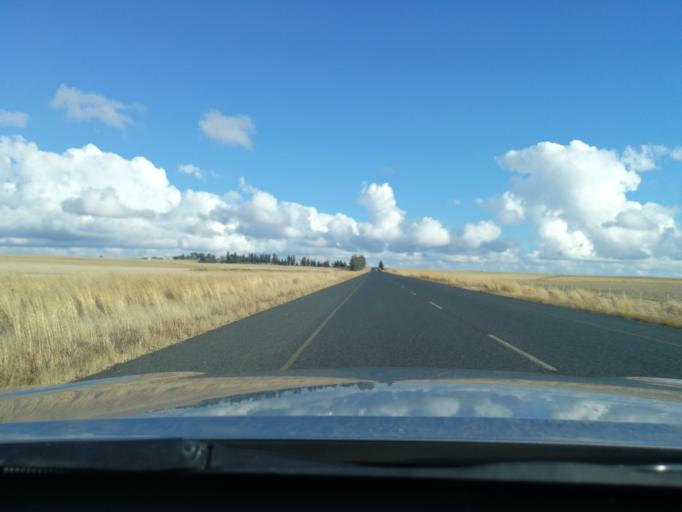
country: ZA
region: Orange Free State
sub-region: Thabo Mofutsanyana District Municipality
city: Bethlehem
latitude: -28.0575
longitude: 28.3641
